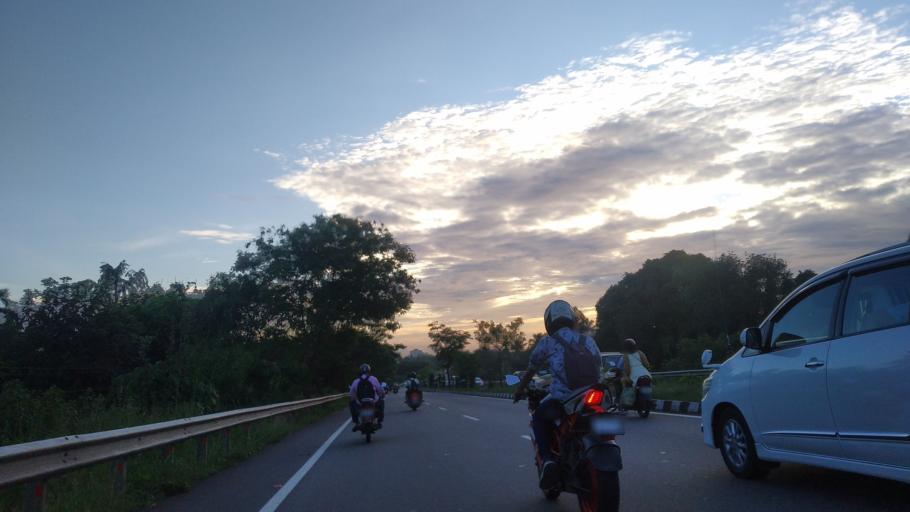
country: IN
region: Kerala
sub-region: Ernakulam
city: Elur
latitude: 10.0665
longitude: 76.2984
